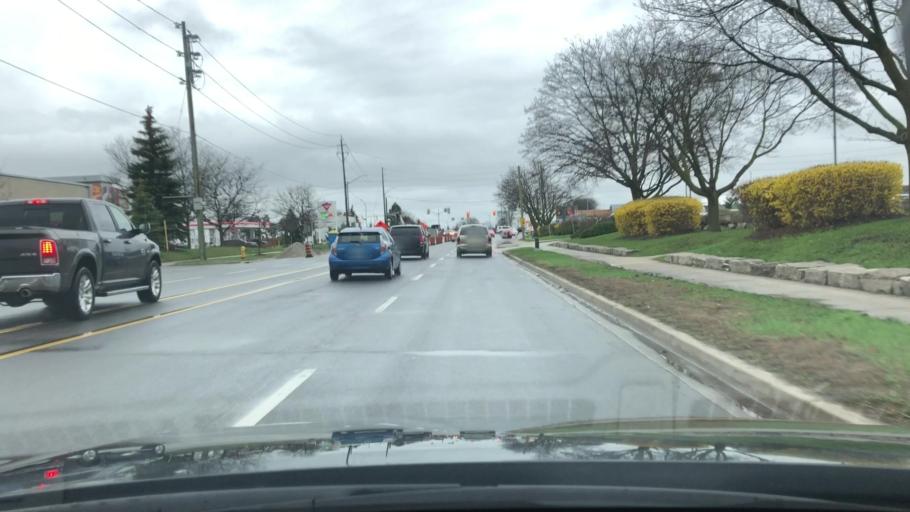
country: CA
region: Ontario
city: Markham
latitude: 43.8733
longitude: -79.2835
